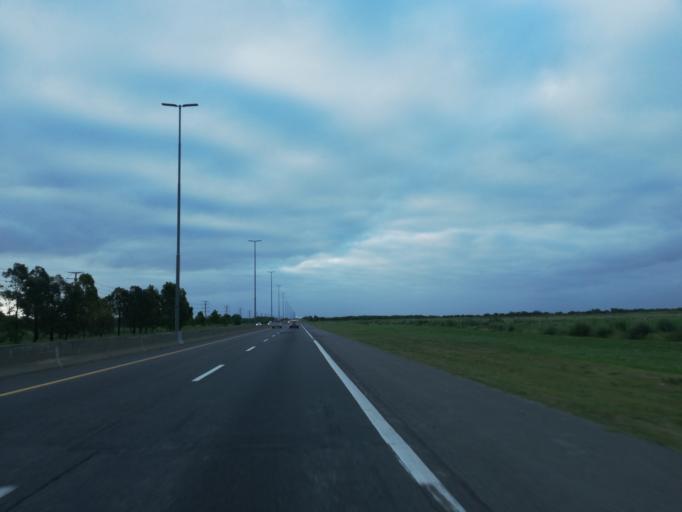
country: AR
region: Buenos Aires
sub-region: Partido de La Plata
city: La Plata
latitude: -34.8266
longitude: -58.0947
